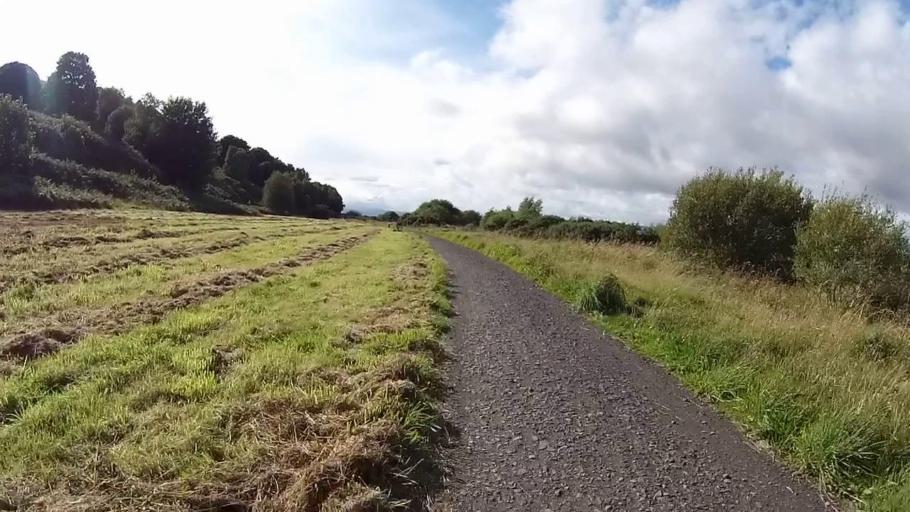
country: GB
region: Scotland
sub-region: Fife
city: Ballingry
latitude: 56.1791
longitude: -3.3421
